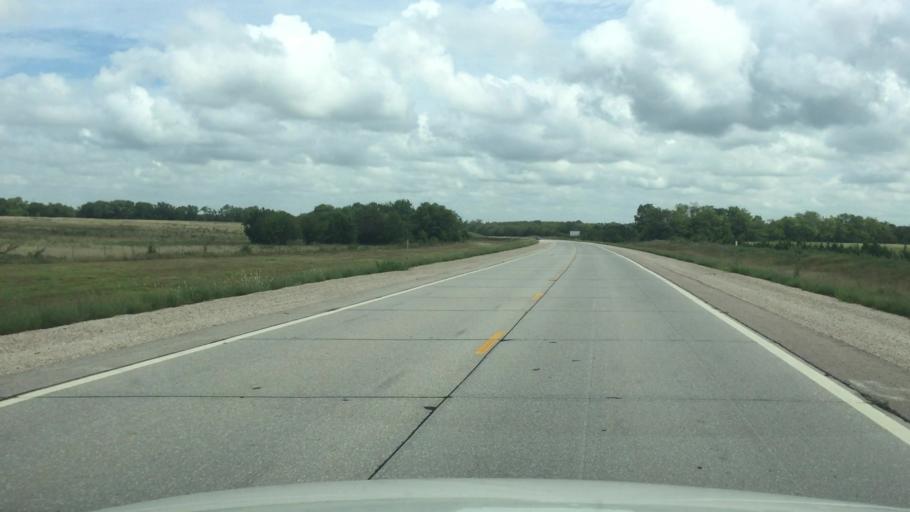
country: US
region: Kansas
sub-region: Allen County
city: Iola
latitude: 37.8942
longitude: -95.3855
